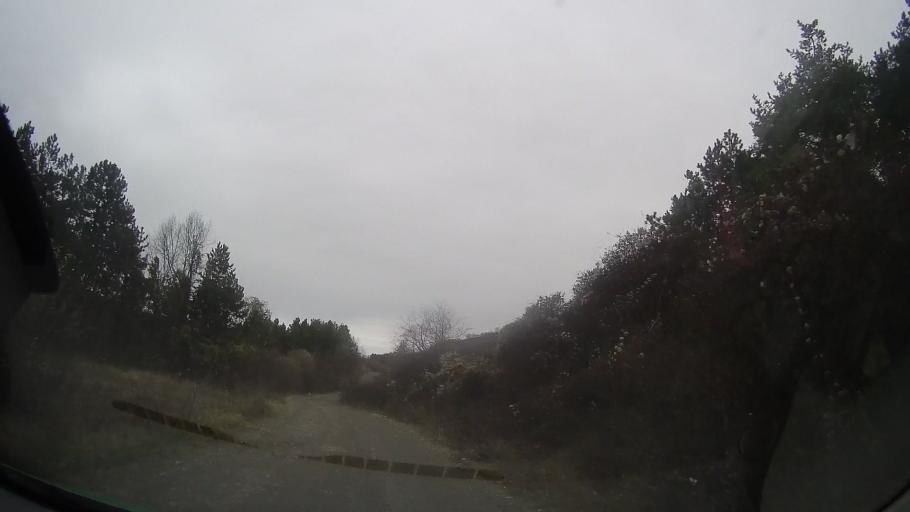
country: RO
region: Mures
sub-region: Comuna Bala
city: Bala
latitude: 46.6803
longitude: 24.4867
